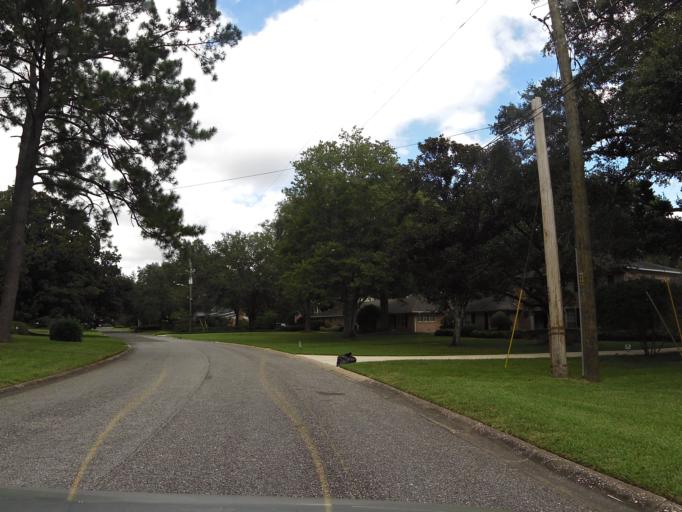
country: US
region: Florida
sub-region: Clay County
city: Bellair-Meadowbrook Terrace
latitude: 30.2551
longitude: -81.7068
